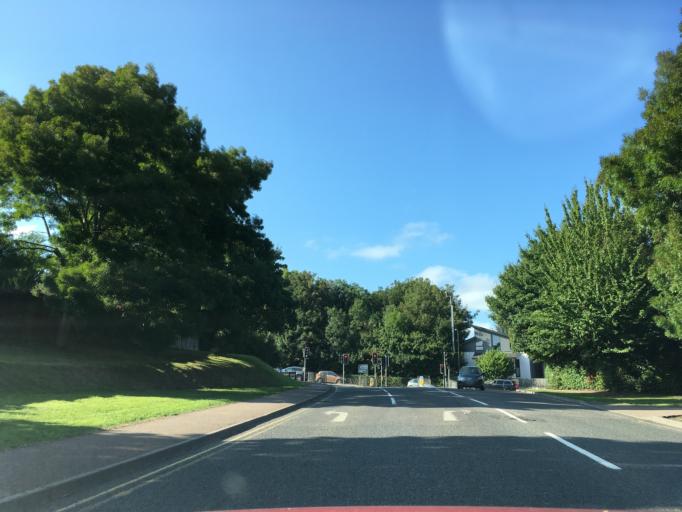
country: GB
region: England
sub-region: Somerset
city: Wells
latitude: 51.2089
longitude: -2.6556
